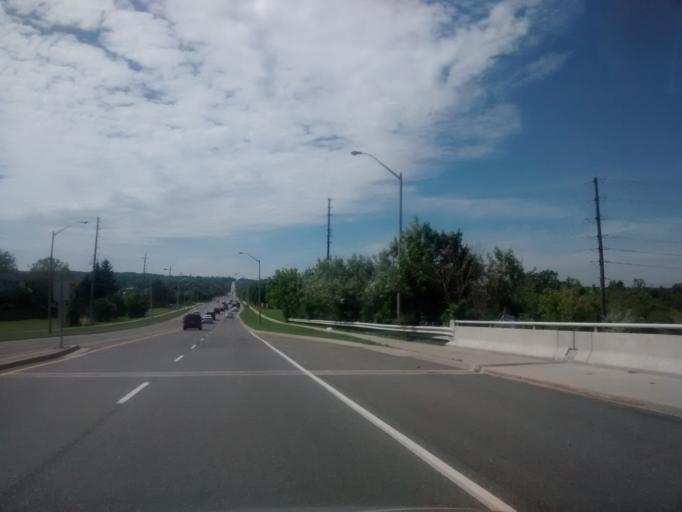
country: CA
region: Ontario
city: Burlington
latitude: 43.3727
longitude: -79.8329
